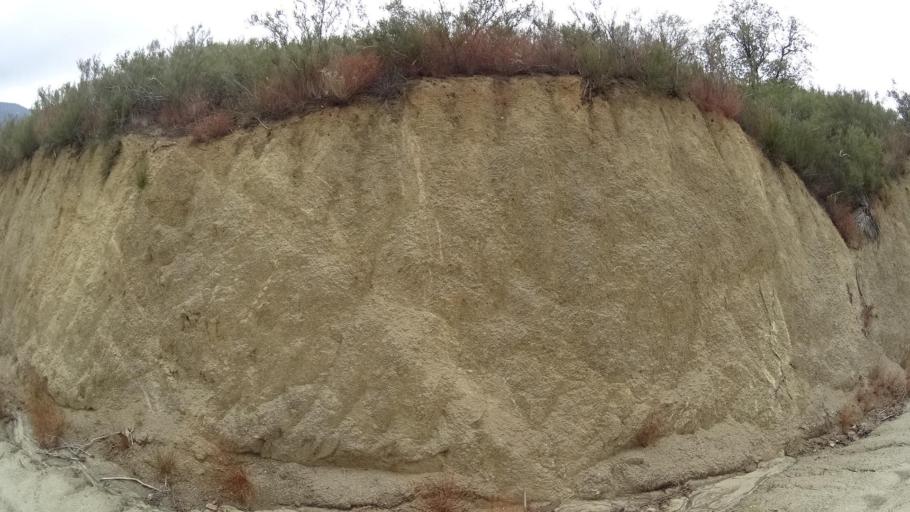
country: US
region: California
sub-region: San Diego County
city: San Diego Country Estates
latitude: 32.9746
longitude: -116.6737
